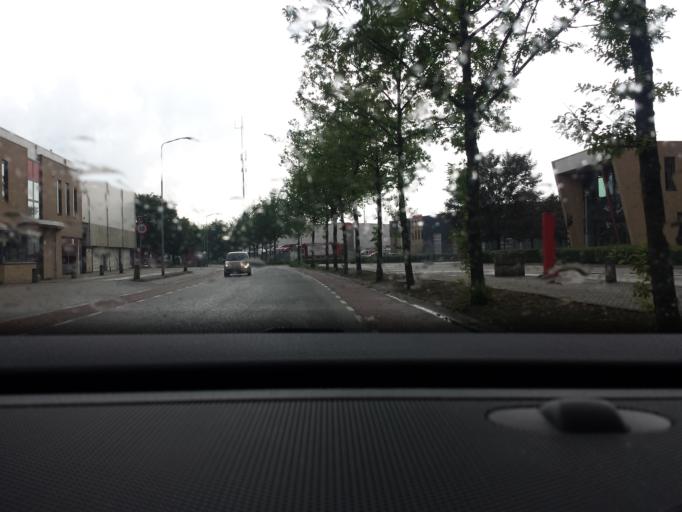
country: NL
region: Gelderland
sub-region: Berkelland
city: Eibergen
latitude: 52.0515
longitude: 6.6224
